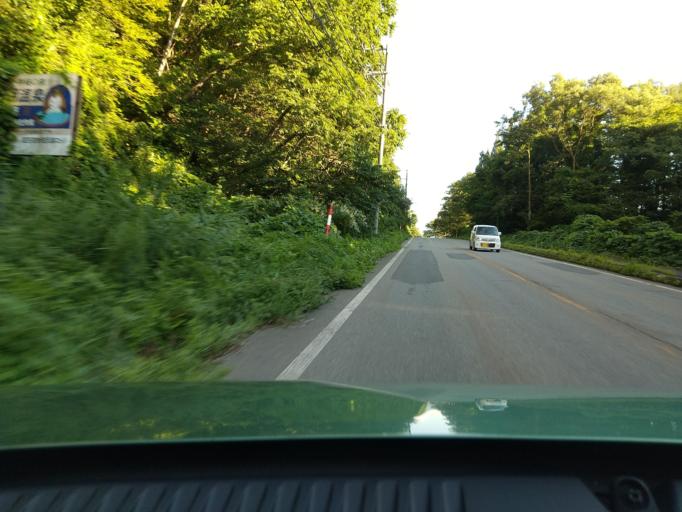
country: JP
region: Akita
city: Kakunodatemachi
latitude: 39.7352
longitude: 140.7183
